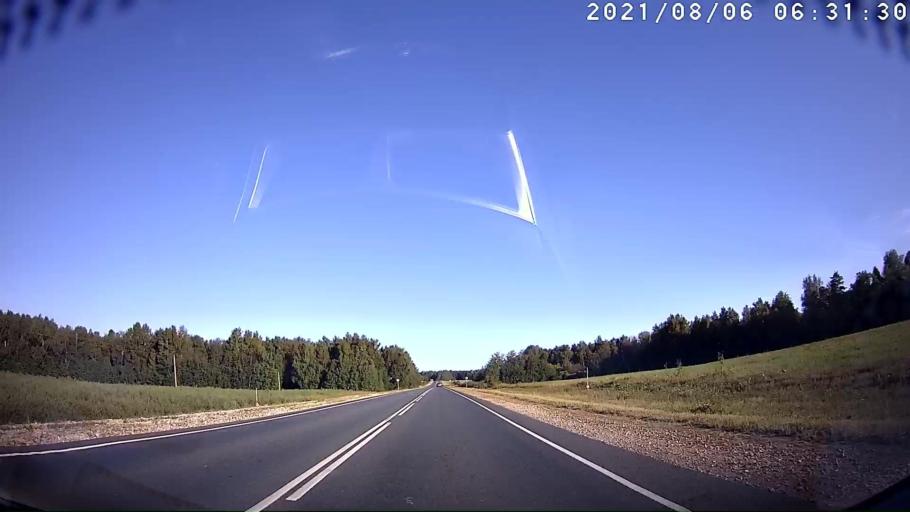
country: RU
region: Mariy-El
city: Krasnogorskiy
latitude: 56.1755
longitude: 48.2743
